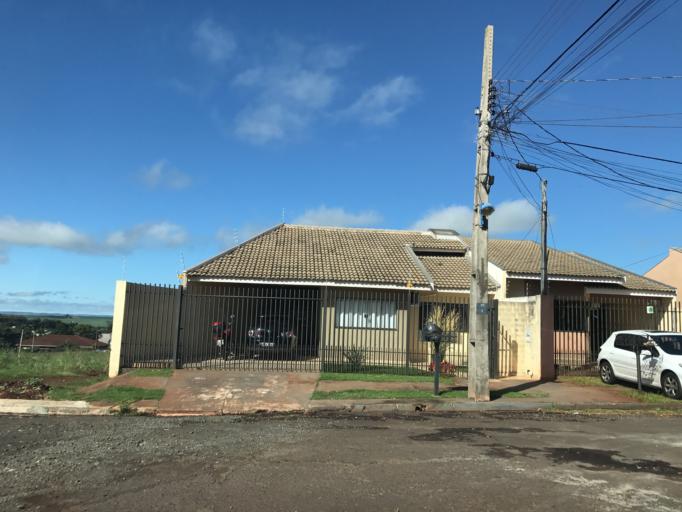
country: BR
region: Parana
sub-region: Maringa
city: Maringa
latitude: -23.4558
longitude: -51.9572
